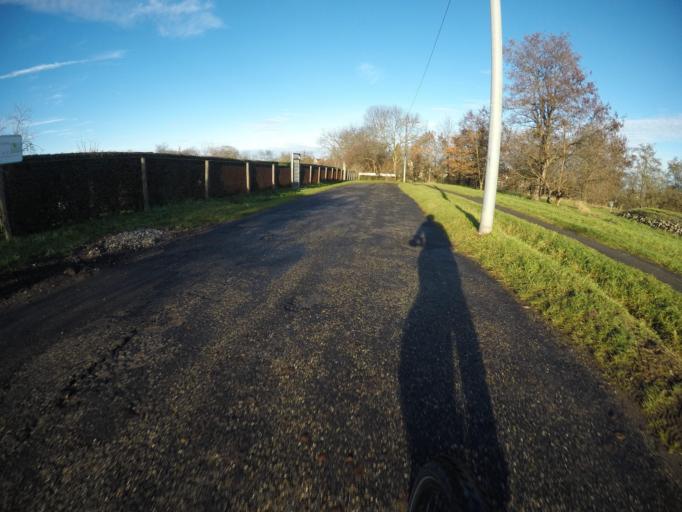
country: DE
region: Baden-Wuerttemberg
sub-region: Regierungsbezirk Stuttgart
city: Stuttgart Feuerbach
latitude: 48.7961
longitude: 9.1655
